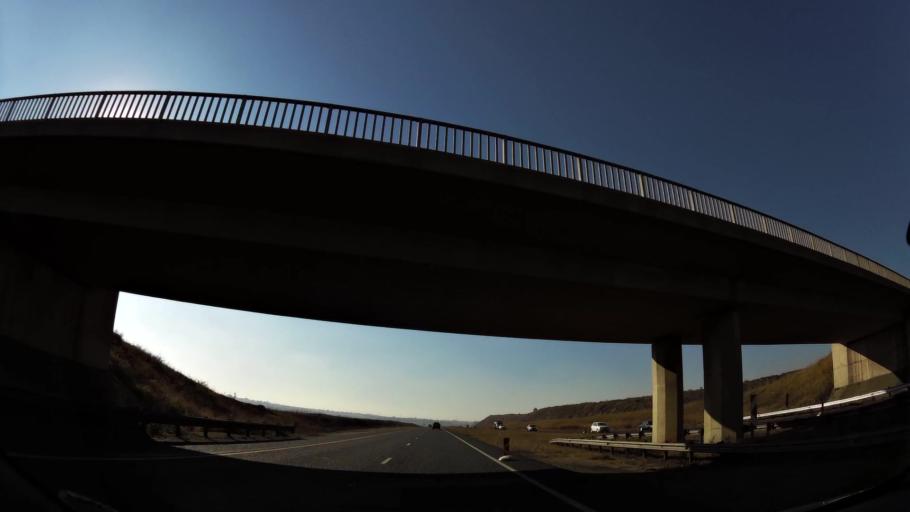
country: ZA
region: Mpumalanga
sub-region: Nkangala District Municipality
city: Witbank
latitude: -26.0220
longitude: 29.0363
